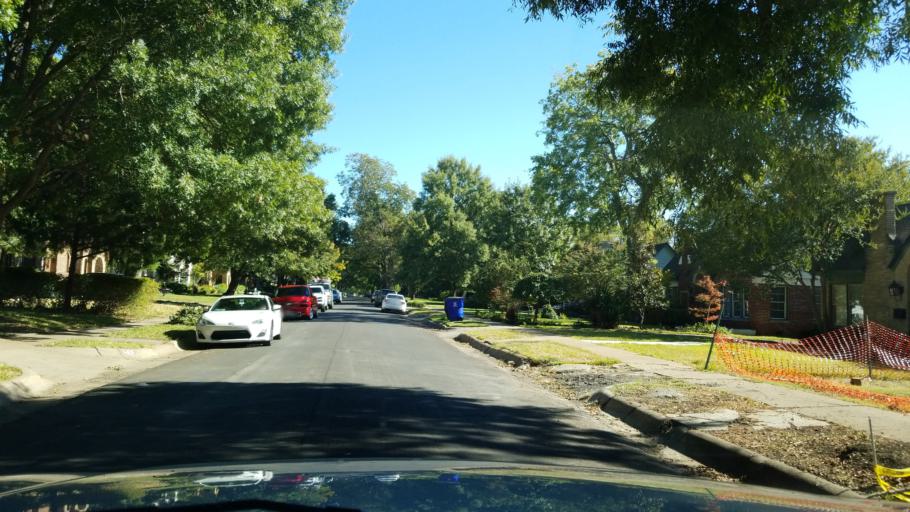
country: US
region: Texas
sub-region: Dallas County
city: Highland Park
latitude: 32.8065
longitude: -96.7451
